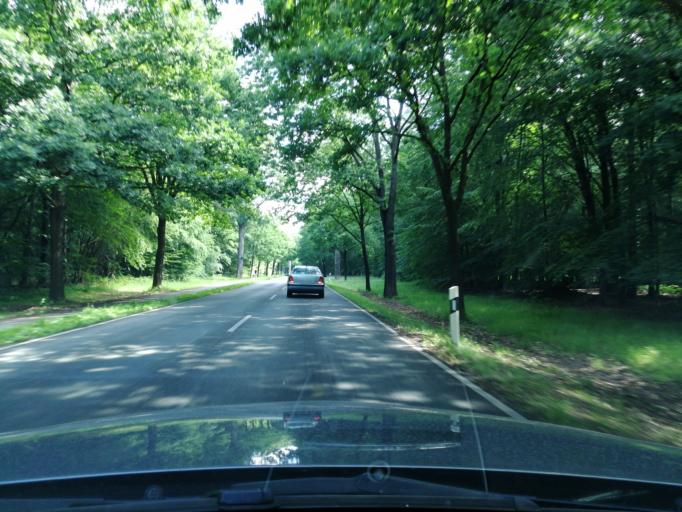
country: DE
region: North Rhine-Westphalia
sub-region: Regierungsbezirk Dusseldorf
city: Kranenburg
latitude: 51.7295
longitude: 6.0673
